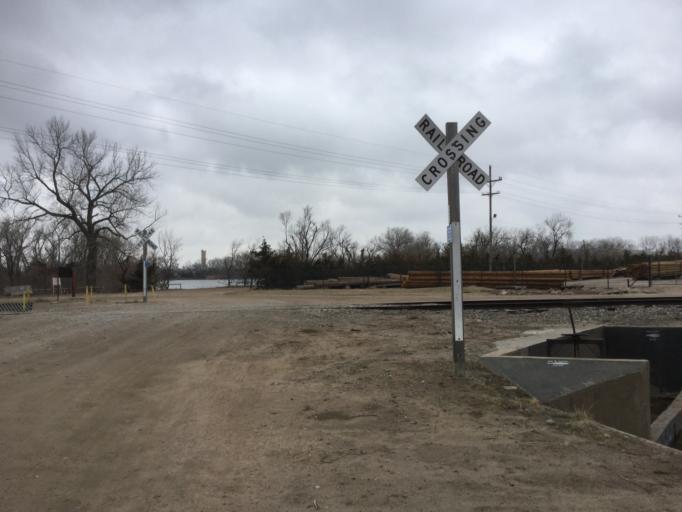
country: US
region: Kansas
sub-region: Barton County
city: Great Bend
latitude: 38.3586
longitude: -98.7782
